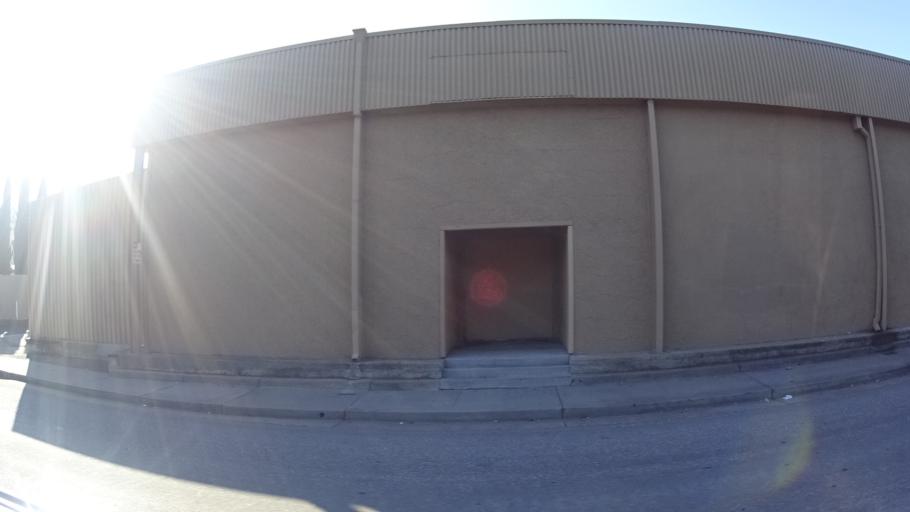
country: US
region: California
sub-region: Santa Clara County
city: Santa Clara
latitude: 37.3508
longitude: -121.9735
